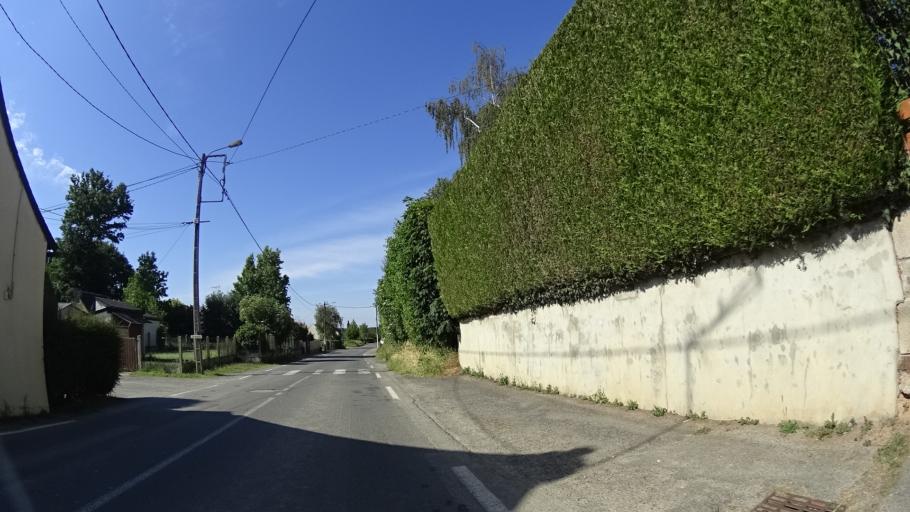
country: FR
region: Brittany
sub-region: Departement d'Ille-et-Vilaine
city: Guipry
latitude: 47.8222
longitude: -1.8444
